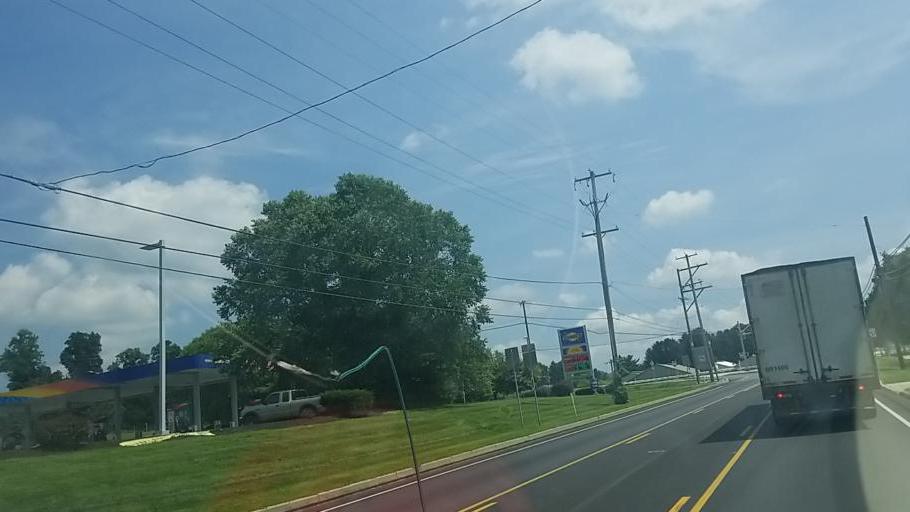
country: US
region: Pennsylvania
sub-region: Chester County
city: Toughkenamon
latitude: 39.8098
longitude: -75.7527
